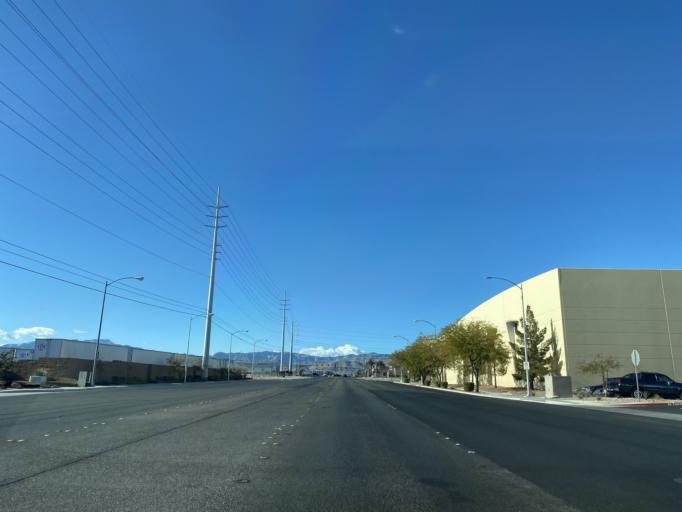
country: US
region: Nevada
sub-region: Clark County
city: Spring Valley
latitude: 36.0707
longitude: -115.2386
